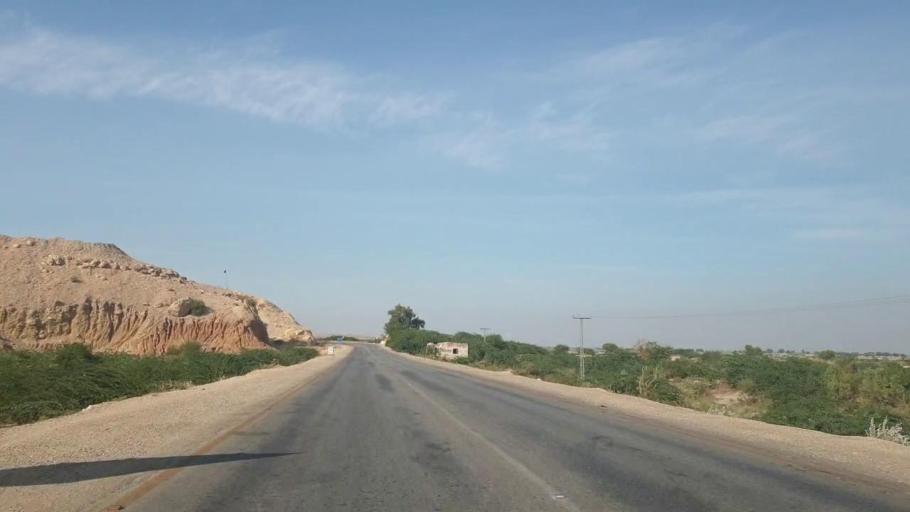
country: PK
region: Sindh
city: Sehwan
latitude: 26.3184
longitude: 67.8887
